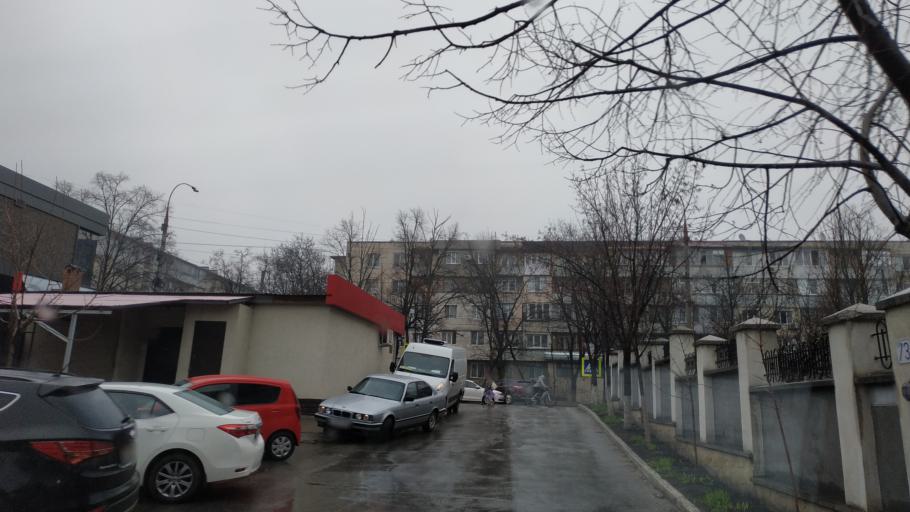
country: MD
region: Chisinau
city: Chisinau
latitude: 47.0224
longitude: 28.7957
